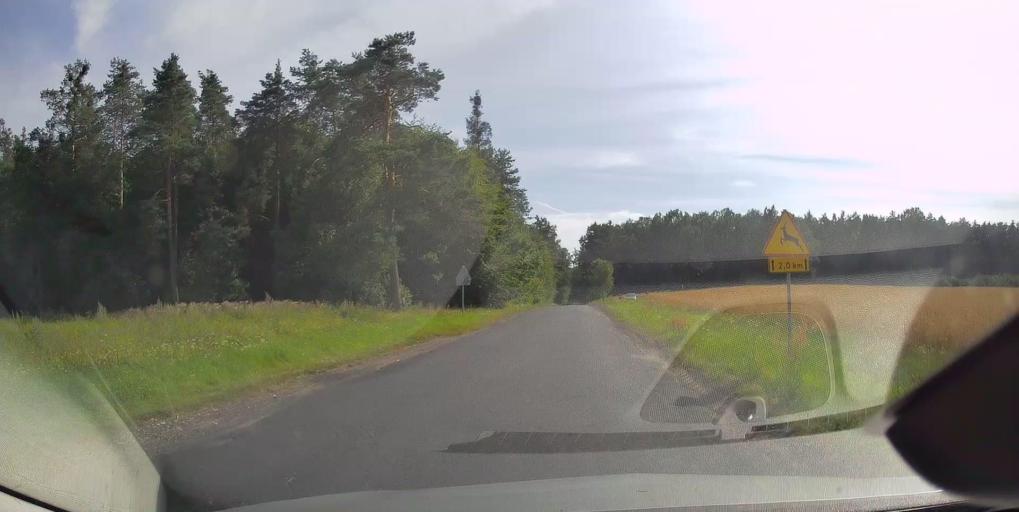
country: PL
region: Lodz Voivodeship
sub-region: Powiat opoczynski
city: Mniszkow
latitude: 51.4423
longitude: 20.0262
